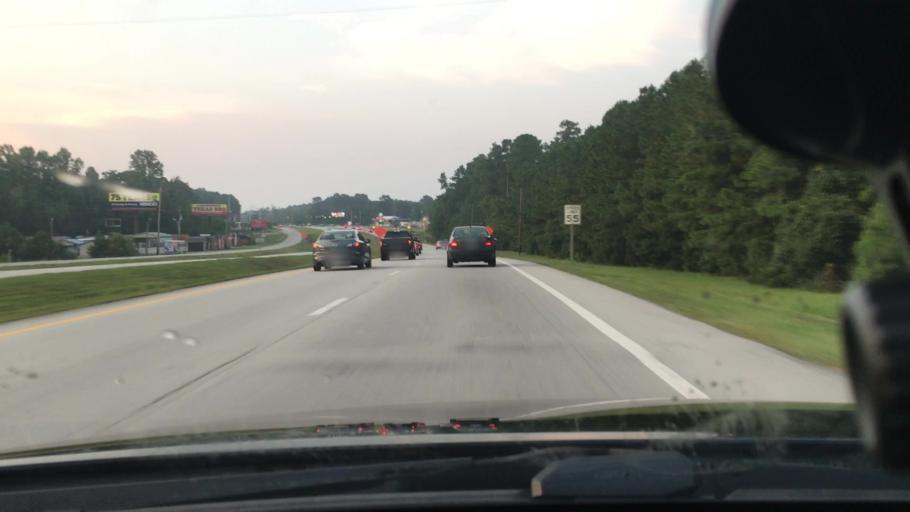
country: US
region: North Carolina
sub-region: Craven County
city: Neuse Forest
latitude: 34.9326
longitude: -76.9492
